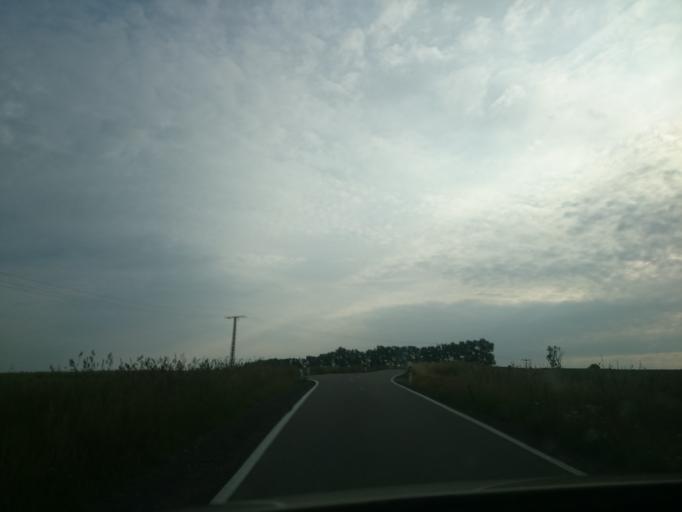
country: DE
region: Saxony
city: Oberschona
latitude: 50.8691
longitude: 13.2578
